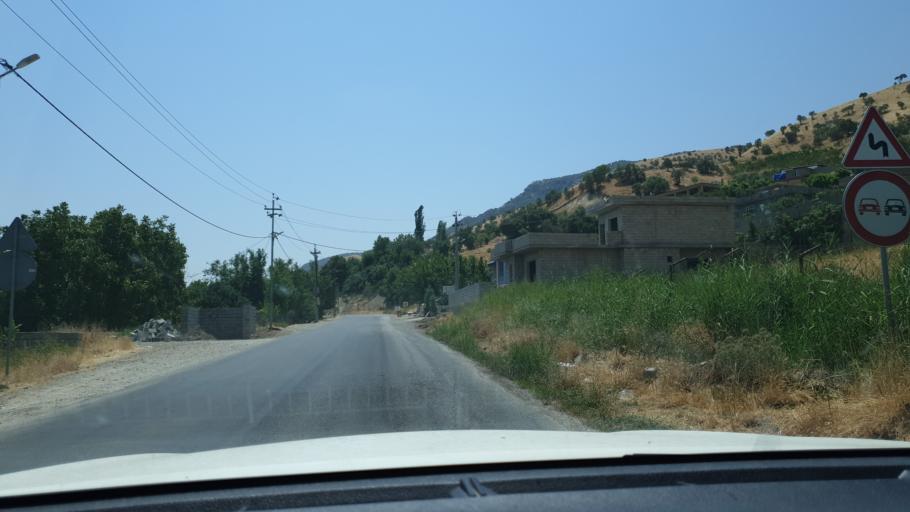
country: IQ
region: Arbil
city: Nahiyat Hiran
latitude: 36.2944
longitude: 44.4753
